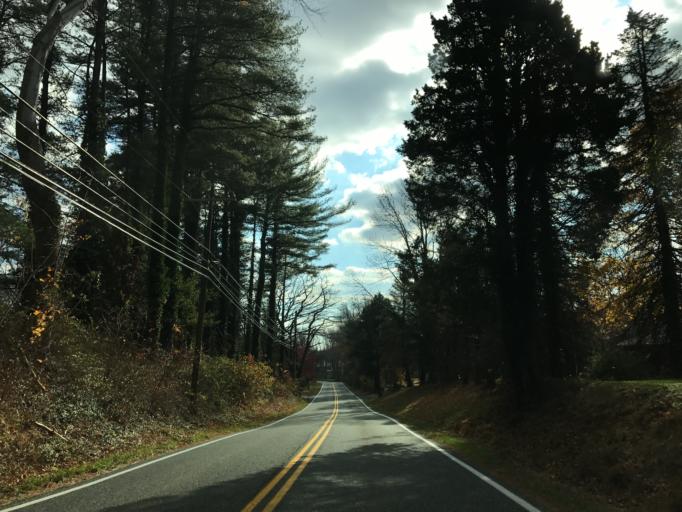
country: US
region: Maryland
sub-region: Harford County
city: Pleasant Hills
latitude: 39.5008
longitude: -76.3736
